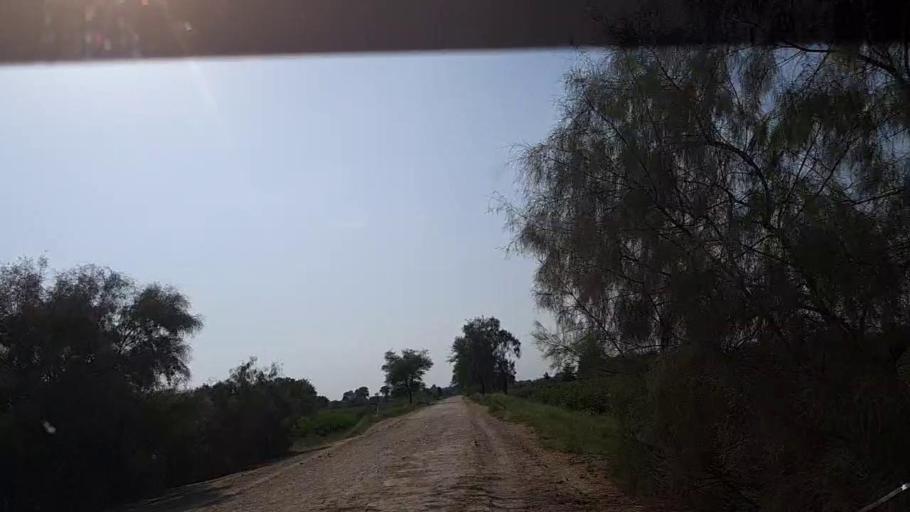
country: PK
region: Sindh
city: Adilpur
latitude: 27.8399
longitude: 69.3139
